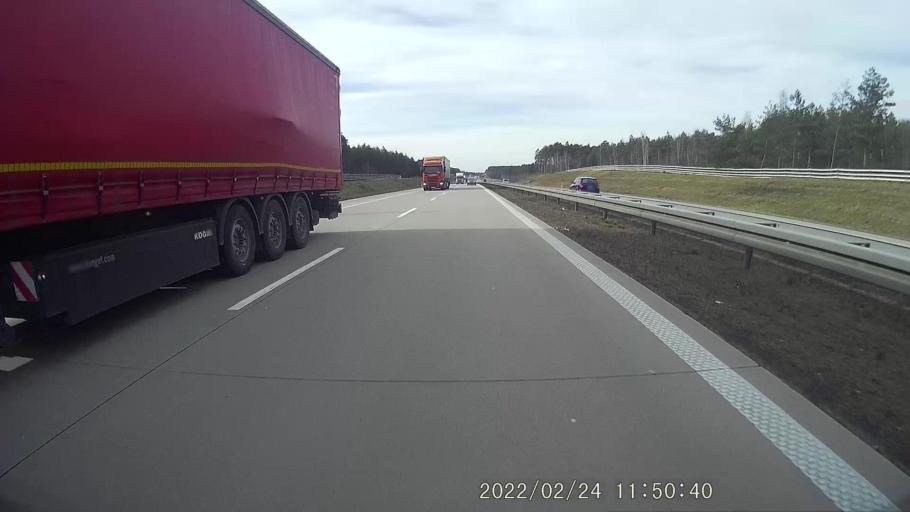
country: PL
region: Lower Silesian Voivodeship
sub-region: Powiat polkowicki
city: Radwanice
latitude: 51.6034
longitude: 15.9644
